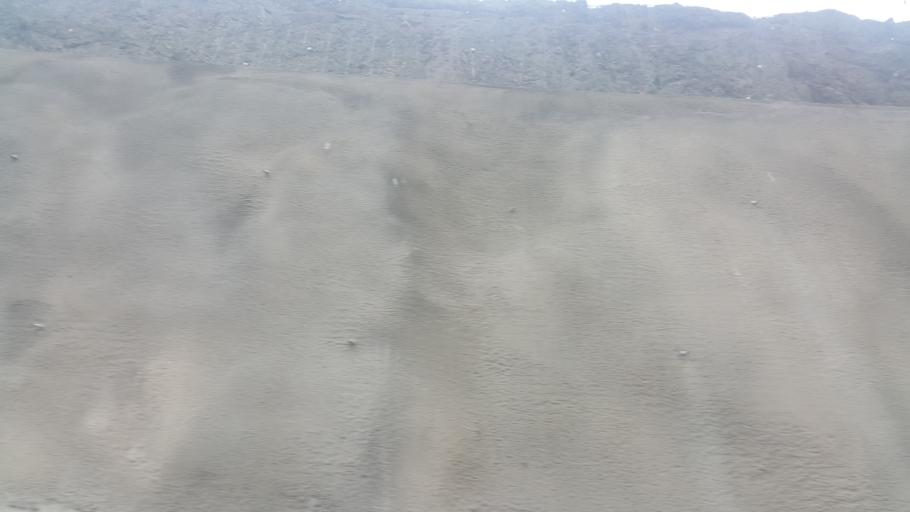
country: TR
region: Nigde
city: Ciftehan
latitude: 37.5482
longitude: 34.7831
